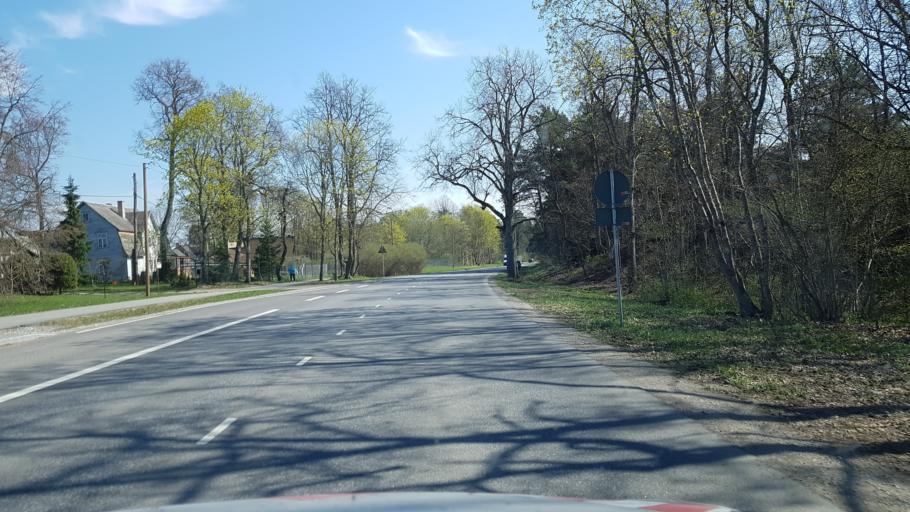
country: EE
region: Harju
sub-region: Keila linn
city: Keila
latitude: 59.3748
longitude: 24.2424
